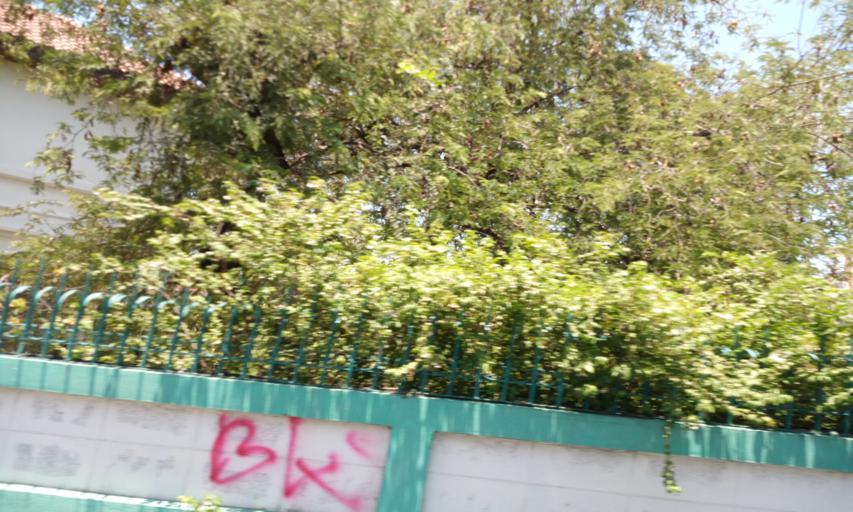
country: TH
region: Bangkok
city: Bang Na
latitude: 13.6067
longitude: 100.7095
